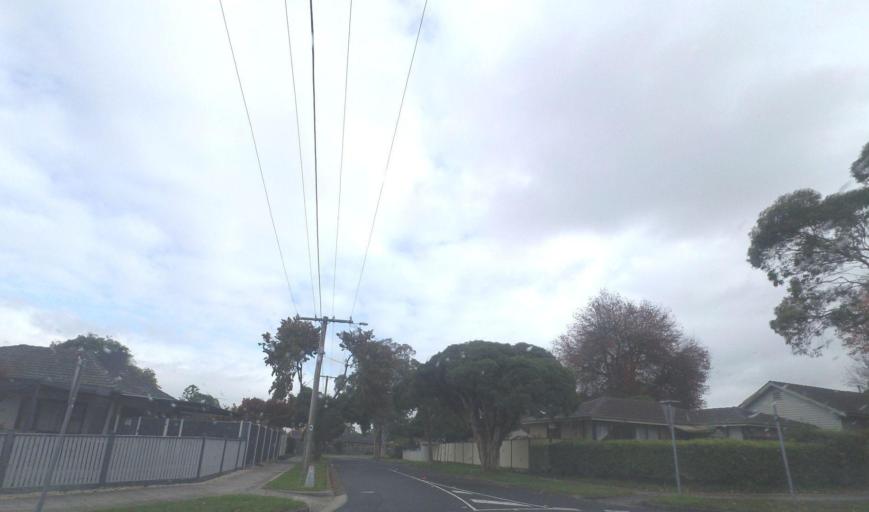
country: AU
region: Victoria
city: Mitcham
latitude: -37.8043
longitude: 145.1867
